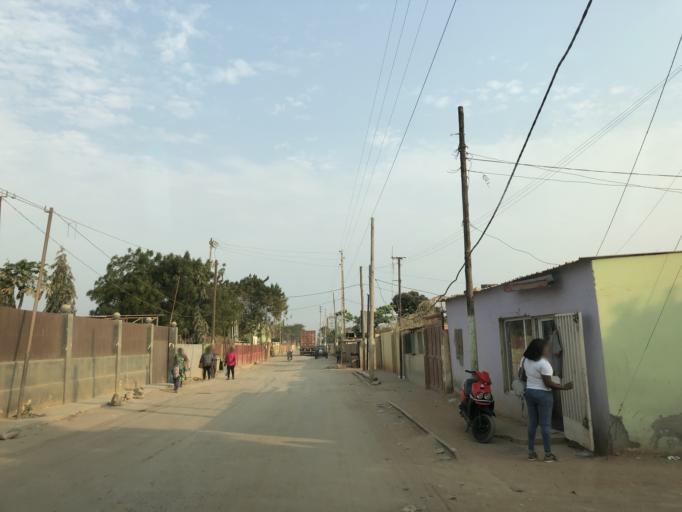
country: AO
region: Luanda
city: Luanda
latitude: -8.9041
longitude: 13.2053
